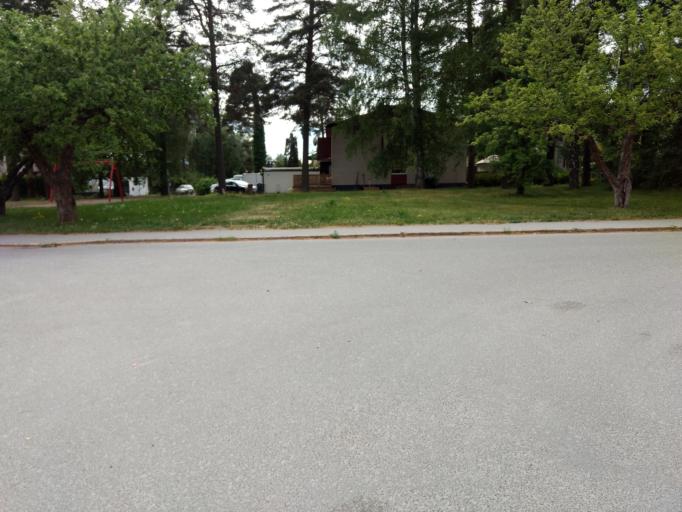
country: SE
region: Stockholm
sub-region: Upplands Vasby Kommun
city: Upplands Vaesby
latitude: 59.5255
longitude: 17.9118
